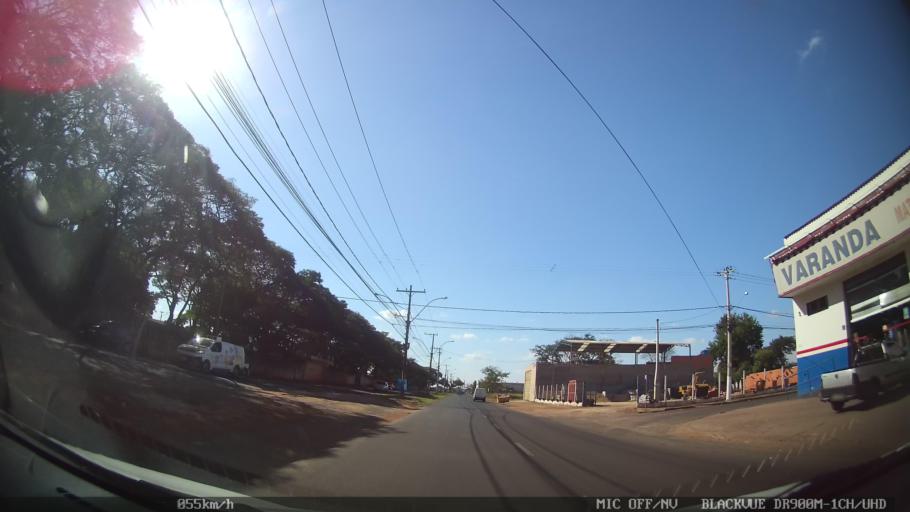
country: BR
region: Sao Paulo
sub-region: Ribeirao Preto
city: Ribeirao Preto
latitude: -21.1536
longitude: -47.7680
